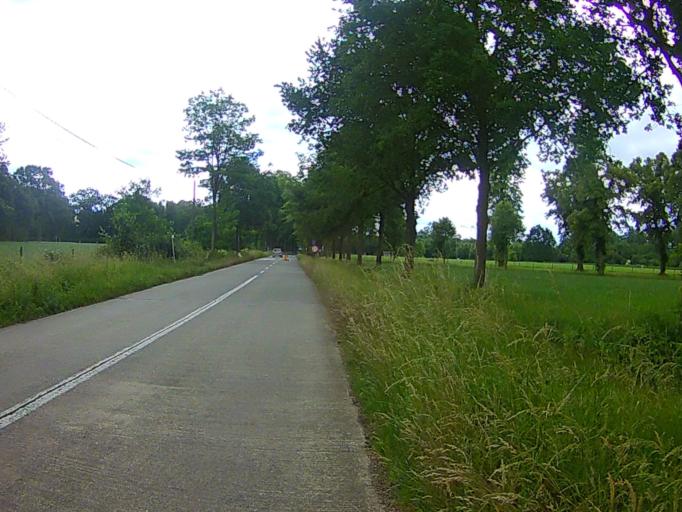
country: BE
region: Flanders
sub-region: Provincie Antwerpen
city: Berlaar
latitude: 51.1238
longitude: 4.6792
